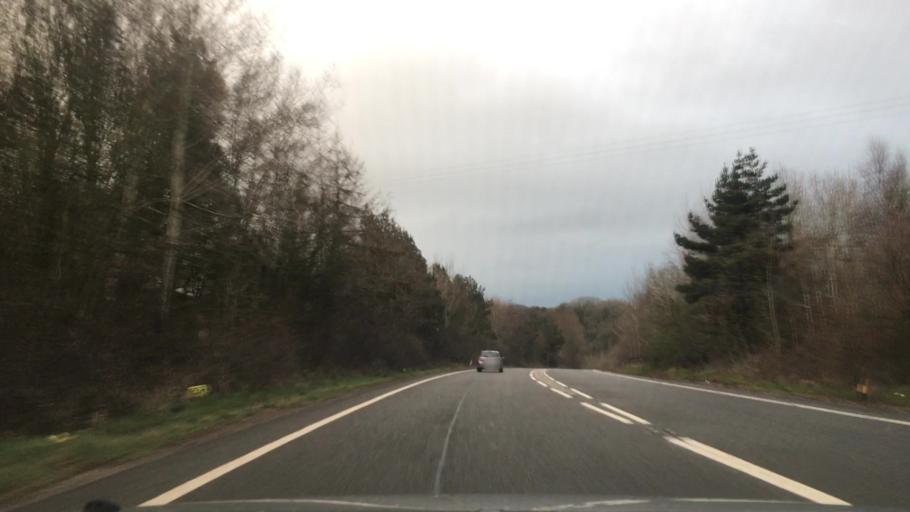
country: GB
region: England
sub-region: Cumbria
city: Askam in Furness
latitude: 54.1602
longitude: -3.2045
